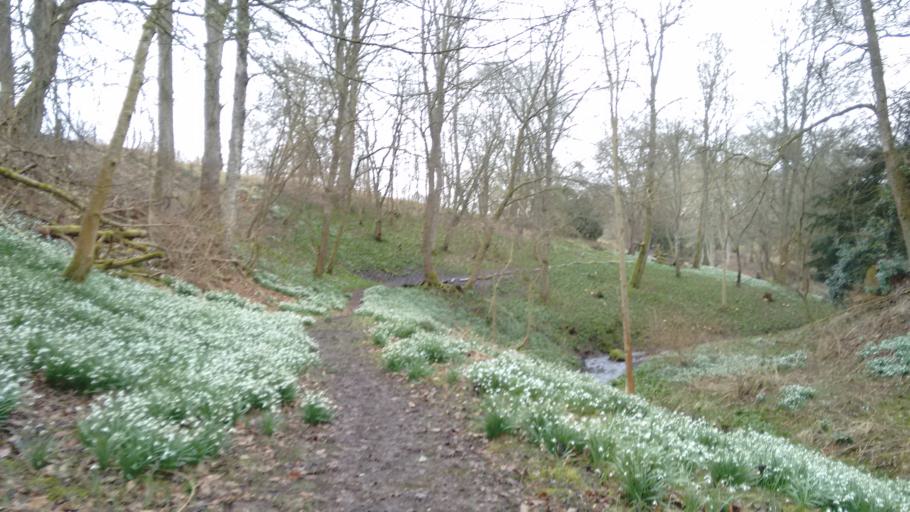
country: GB
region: Scotland
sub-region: Perth and Kinross
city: Perth
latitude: 56.4200
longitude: -3.4370
